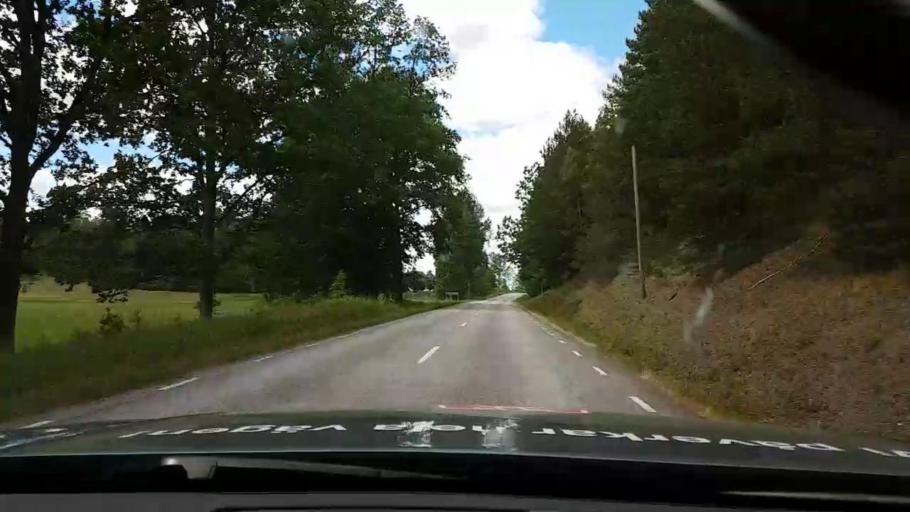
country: SE
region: Kalmar
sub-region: Vasterviks Kommun
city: Overum
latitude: 58.0761
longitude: 16.3610
